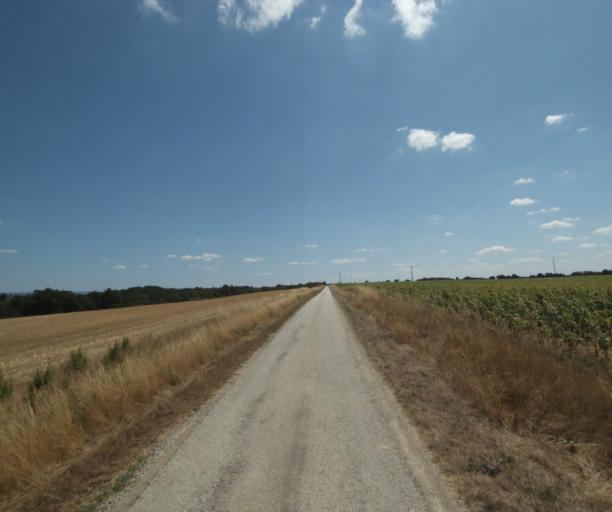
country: FR
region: Midi-Pyrenees
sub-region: Departement de la Haute-Garonne
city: Auriac-sur-Vendinelle
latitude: 43.4982
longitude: 1.8518
